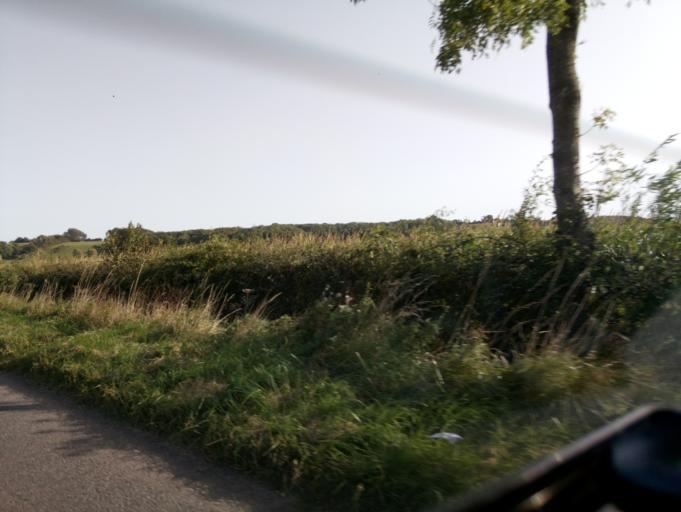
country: GB
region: England
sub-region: Gloucestershire
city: Gloucester
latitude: 51.9599
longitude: -2.2870
